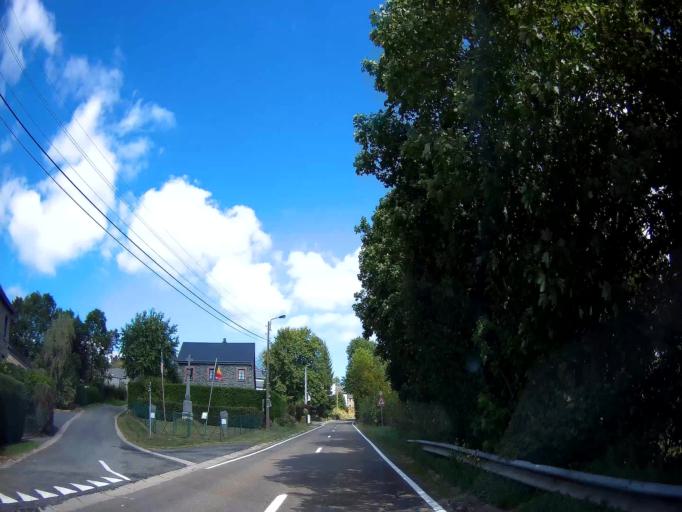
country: BE
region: Wallonia
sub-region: Province du Luxembourg
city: Bertogne
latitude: 50.0503
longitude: 5.6882
